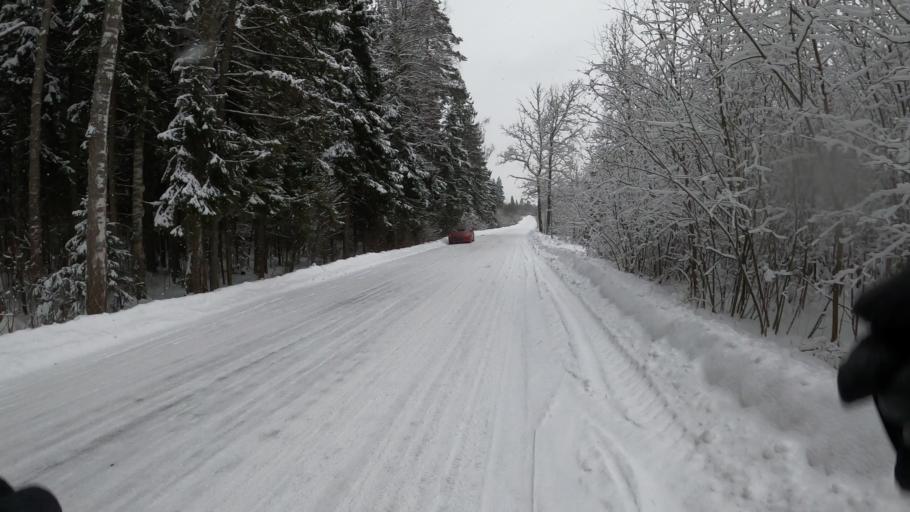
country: RU
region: Moskovskaya
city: Firsanovka
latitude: 55.9212
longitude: 37.2118
